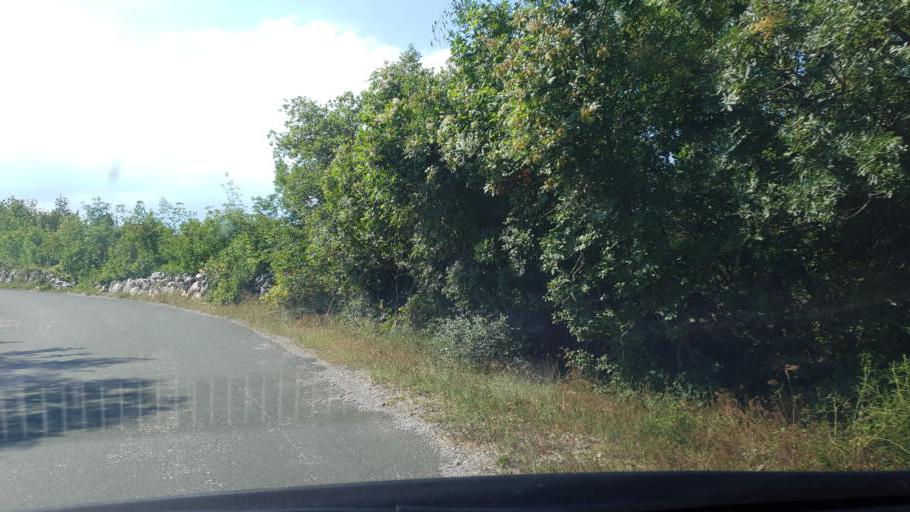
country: HR
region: Primorsko-Goranska
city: Omisalj
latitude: 45.1939
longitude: 14.5817
